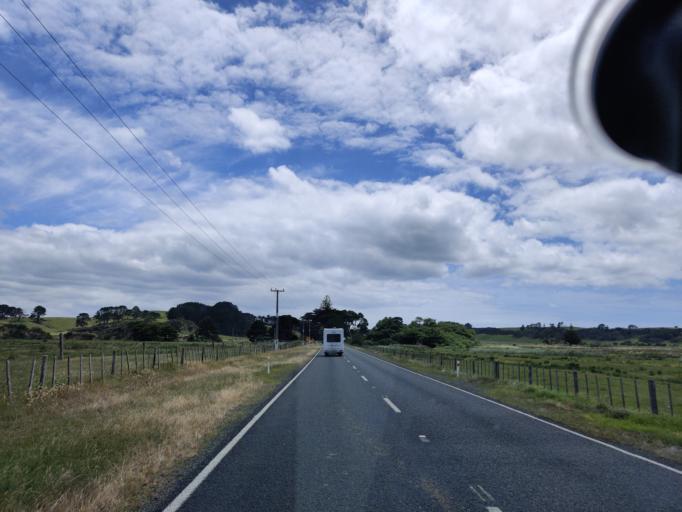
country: NZ
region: Northland
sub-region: Far North District
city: Kaitaia
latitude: -34.7623
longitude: 173.0762
